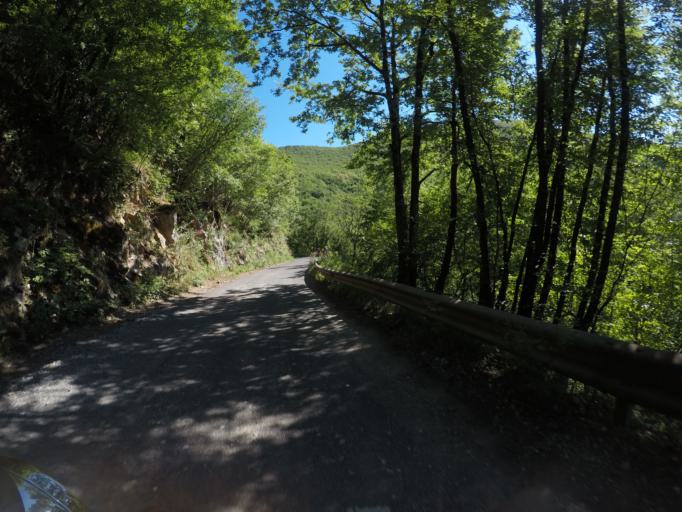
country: IT
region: Tuscany
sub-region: Provincia di Massa-Carrara
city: Fosdinovo
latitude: 44.1313
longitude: 10.0680
